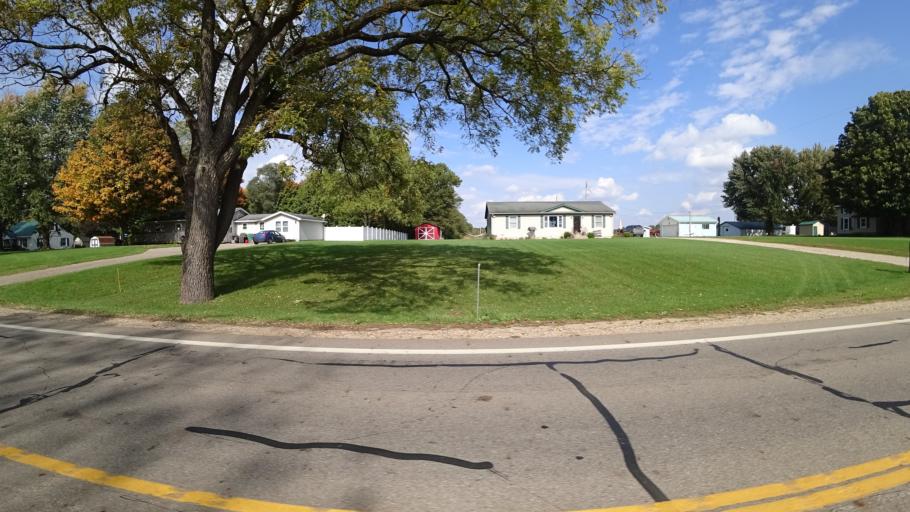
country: US
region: Michigan
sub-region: Saint Joseph County
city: Three Rivers
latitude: 41.9256
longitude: -85.6197
